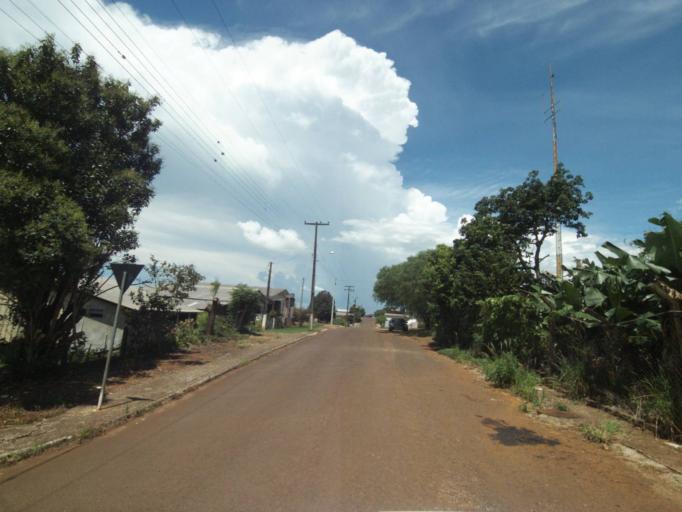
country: BR
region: Parana
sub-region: Guaraniacu
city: Guaraniacu
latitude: -25.0940
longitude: -52.8755
